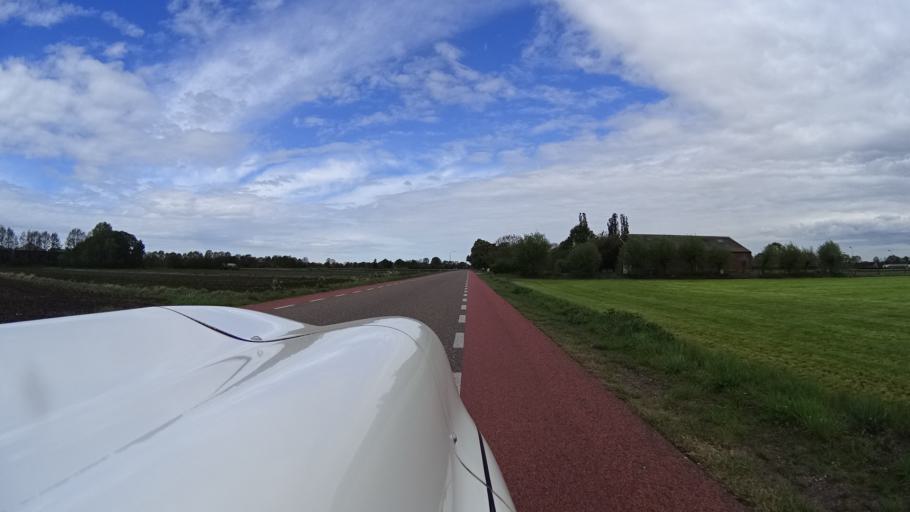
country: NL
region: North Brabant
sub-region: Gemeente Sint Anthonis
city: Sint Anthonis
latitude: 51.5866
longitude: 5.8891
